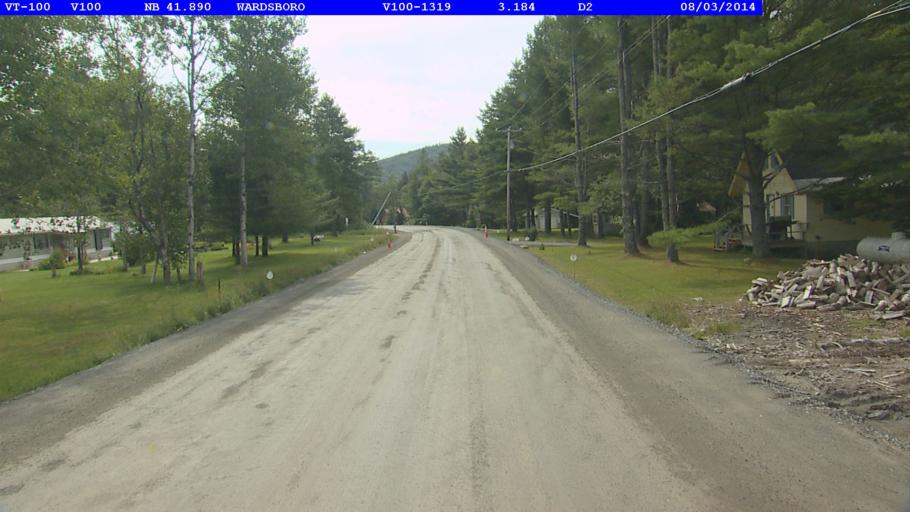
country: US
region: Vermont
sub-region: Windham County
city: Dover
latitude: 43.0312
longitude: -72.8379
